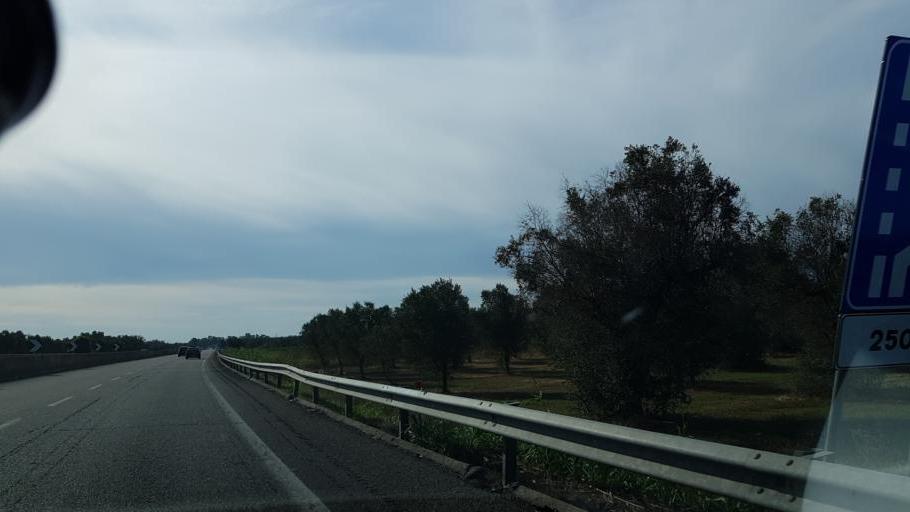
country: IT
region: Apulia
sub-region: Provincia di Brindisi
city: San Pietro Vernotico
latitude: 40.5327
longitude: 18.0093
